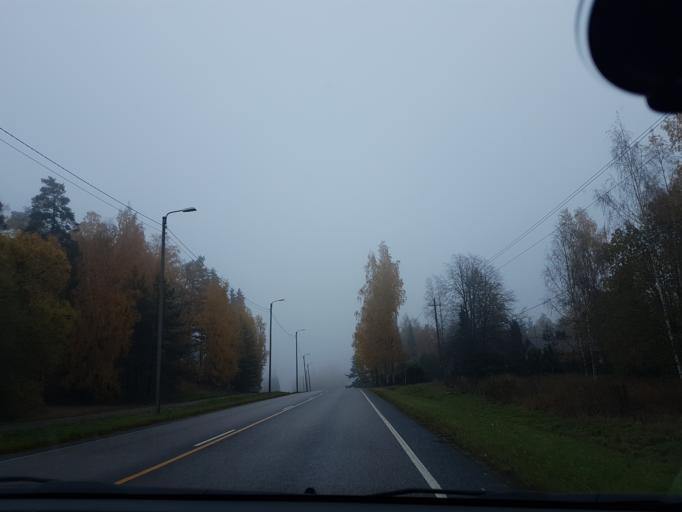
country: FI
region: Uusimaa
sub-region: Helsinki
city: Jaervenpaeae
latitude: 60.4350
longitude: 25.0643
